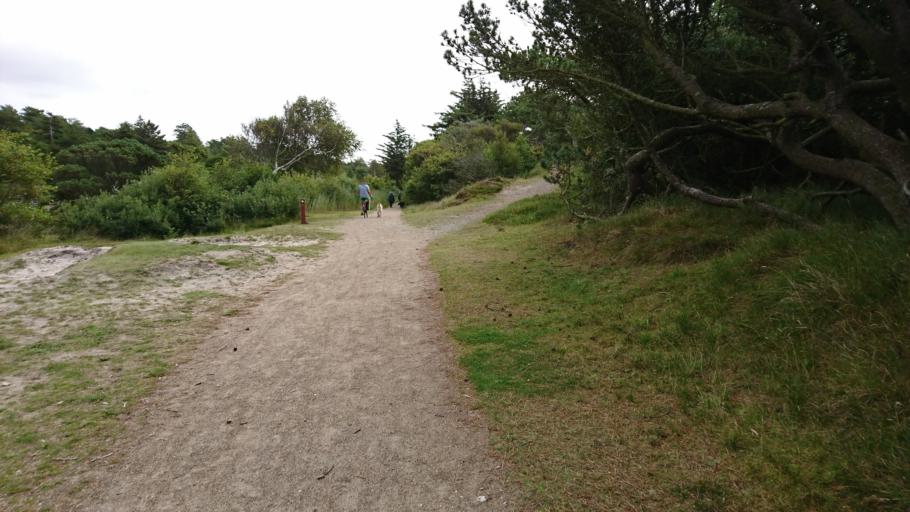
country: DK
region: South Denmark
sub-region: Fano Kommune
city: Nordby
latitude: 55.3884
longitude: 8.4091
